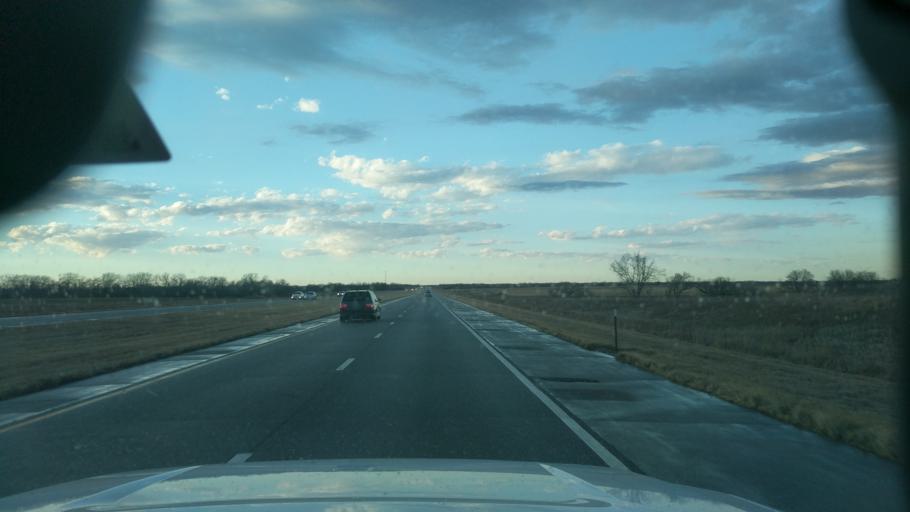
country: US
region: Kansas
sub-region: Harvey County
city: Hesston
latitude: 38.1757
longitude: -97.4493
